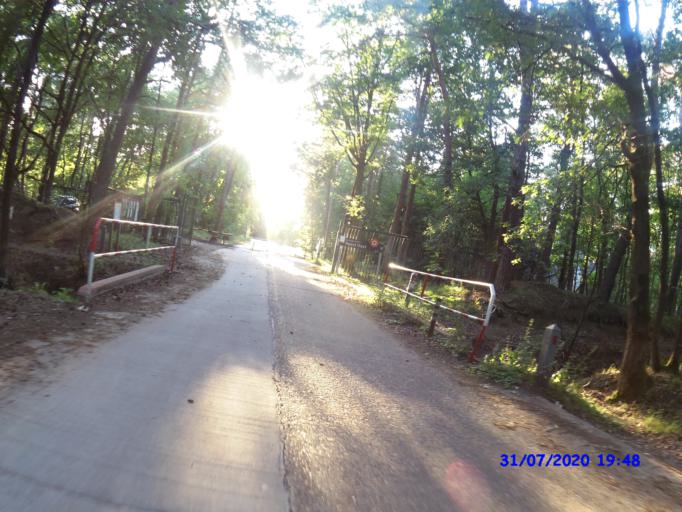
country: BE
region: Flanders
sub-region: Provincie Antwerpen
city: Kasterlee
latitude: 51.2389
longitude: 4.9448
